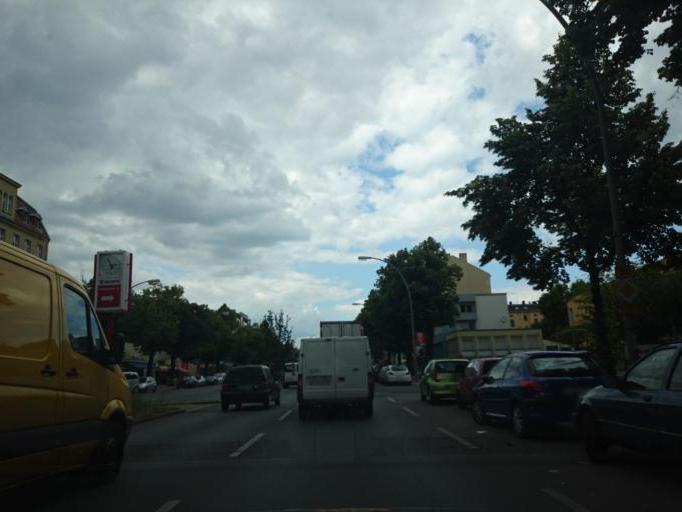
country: DE
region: Berlin
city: Tempelhof Bezirk
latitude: 52.4668
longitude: 13.3857
